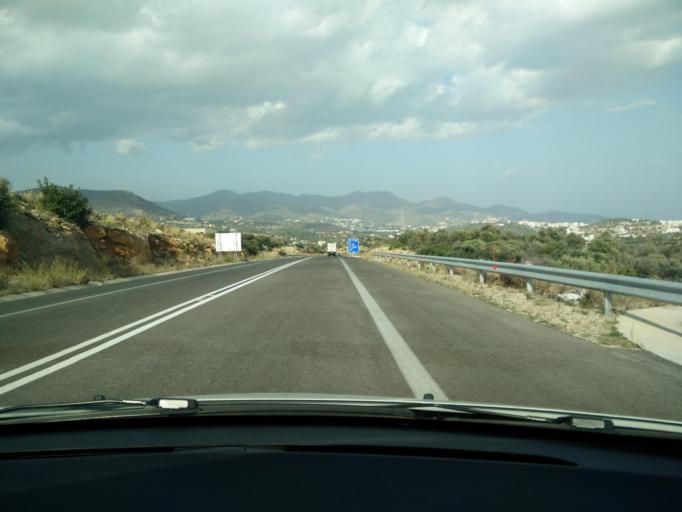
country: GR
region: Crete
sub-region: Nomos Lasithiou
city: Agios Nikolaos
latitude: 35.1750
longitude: 25.7008
